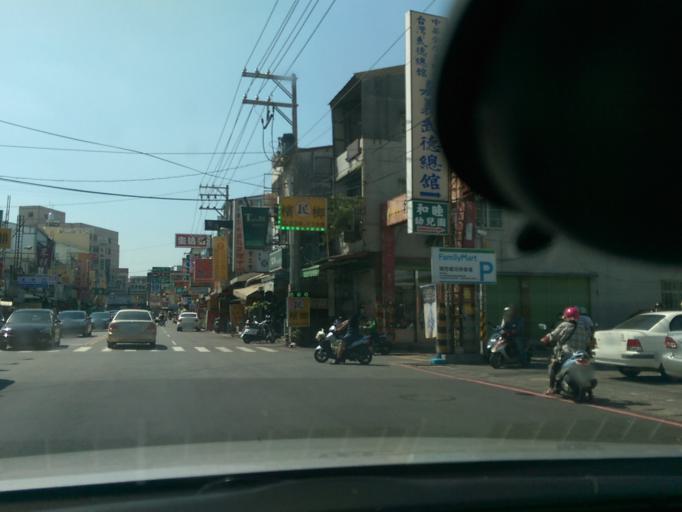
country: TW
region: Taiwan
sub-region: Chiayi
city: Jiayi Shi
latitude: 23.4533
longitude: 120.4600
